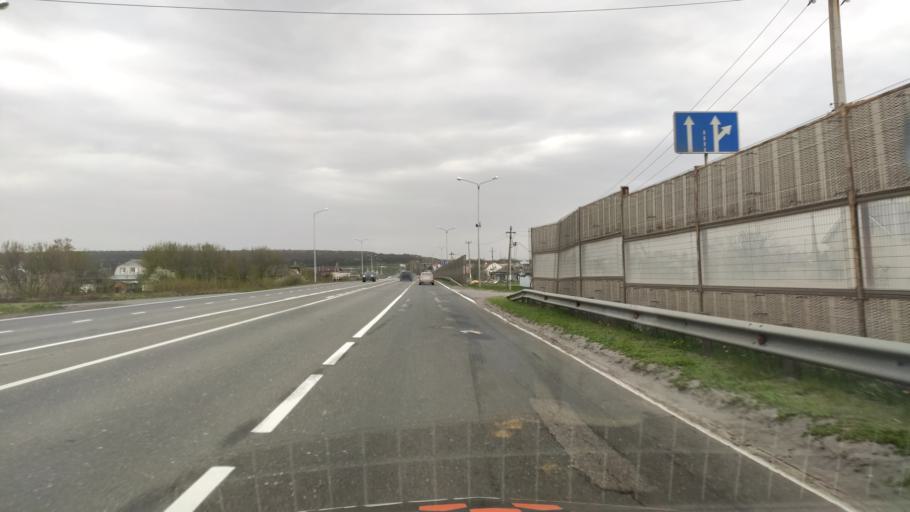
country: RU
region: Belgorod
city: Staryy Oskol
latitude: 51.3440
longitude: 37.8118
